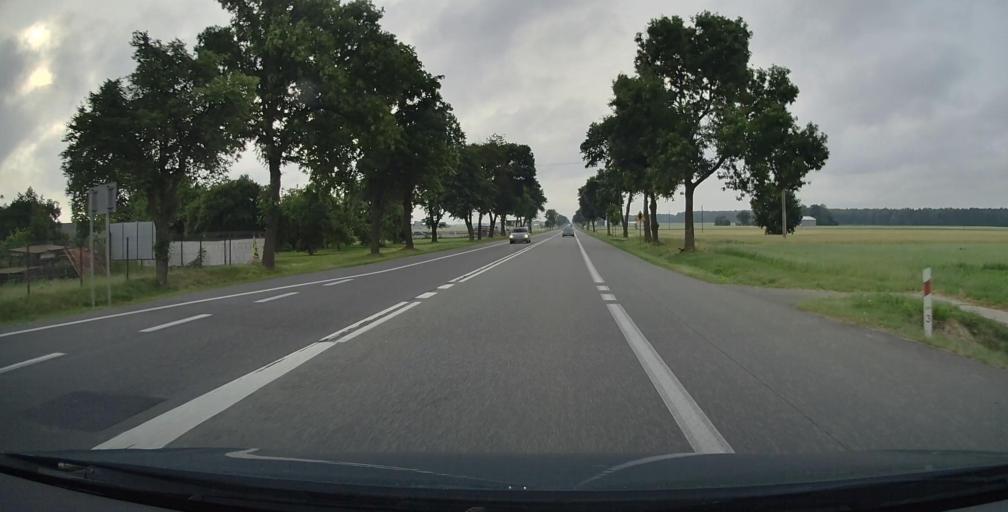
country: PL
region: Masovian Voivodeship
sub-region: Powiat siedlecki
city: Zbuczyn
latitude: 52.1071
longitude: 22.3890
